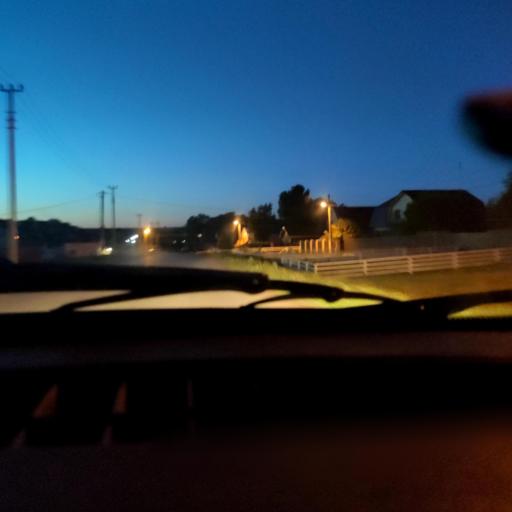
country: RU
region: Bashkortostan
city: Avdon
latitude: 54.6986
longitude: 55.7512
